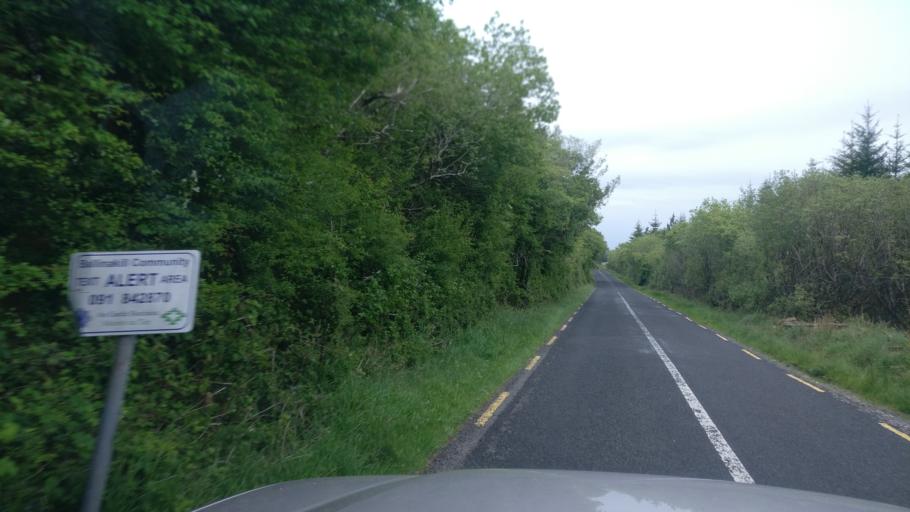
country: IE
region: Connaught
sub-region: County Galway
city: Loughrea
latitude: 53.0766
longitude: -8.5527
